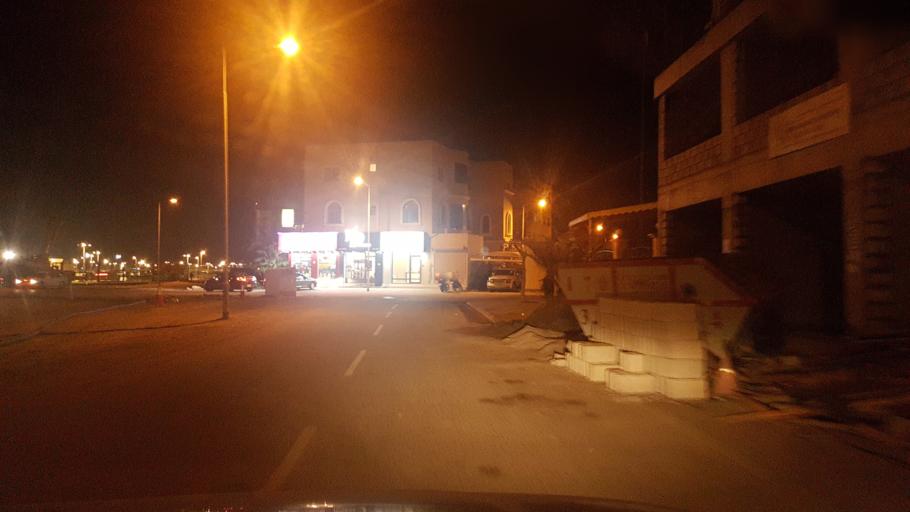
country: BH
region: Muharraq
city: Al Hadd
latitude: 26.2645
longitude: 50.6546
